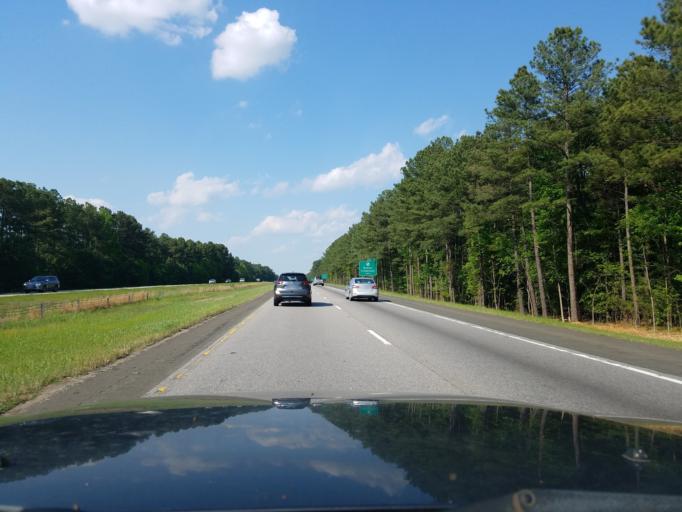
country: US
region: North Carolina
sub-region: Granville County
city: Butner
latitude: 36.1317
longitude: -78.7380
